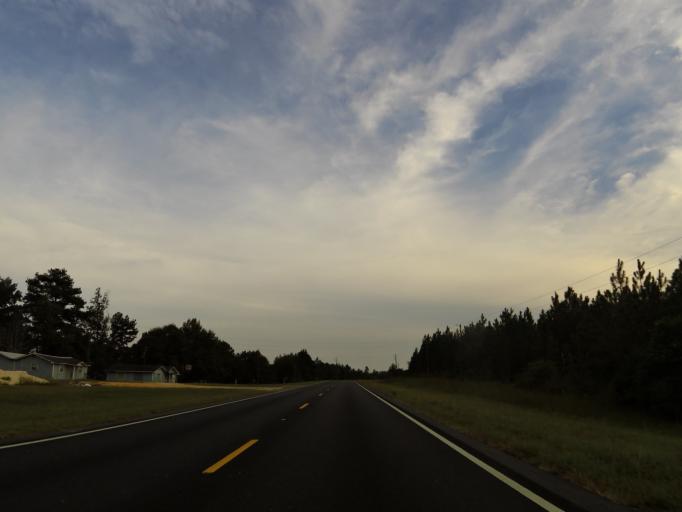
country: US
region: Alabama
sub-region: Escambia County
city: Atmore
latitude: 31.2358
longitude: -87.4825
